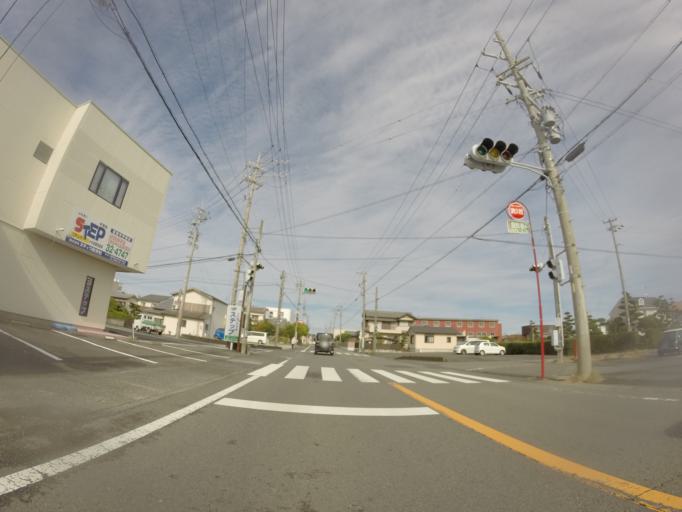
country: JP
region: Shizuoka
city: Shimada
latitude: 34.7707
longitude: 138.2543
